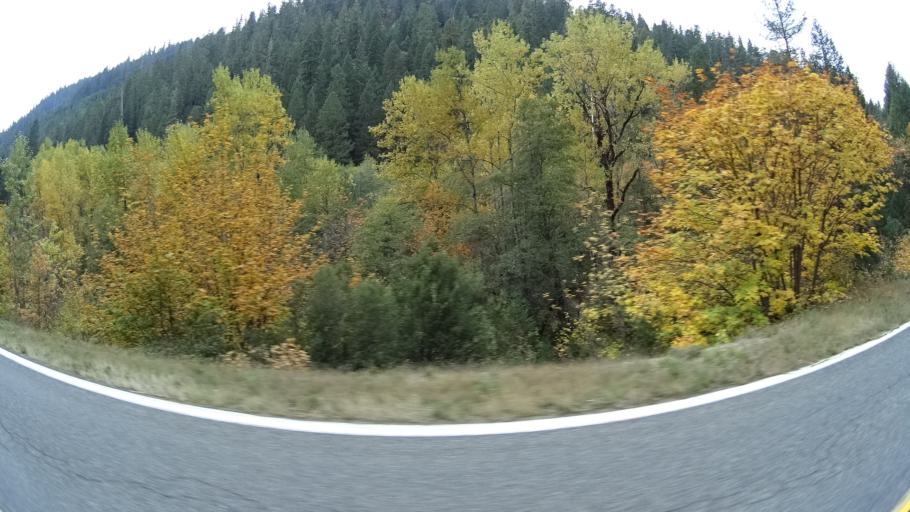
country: US
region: California
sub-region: Siskiyou County
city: Happy Camp
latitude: 41.9051
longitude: -123.4407
